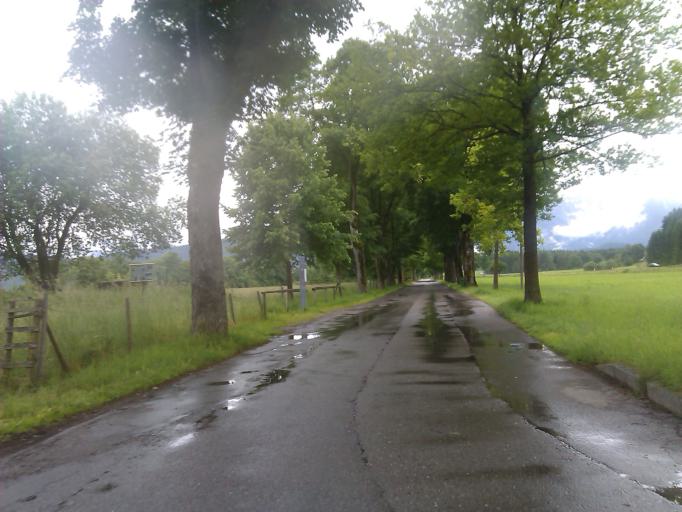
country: DE
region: Bavaria
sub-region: Swabia
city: Fuessen
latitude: 47.5975
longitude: 10.7124
